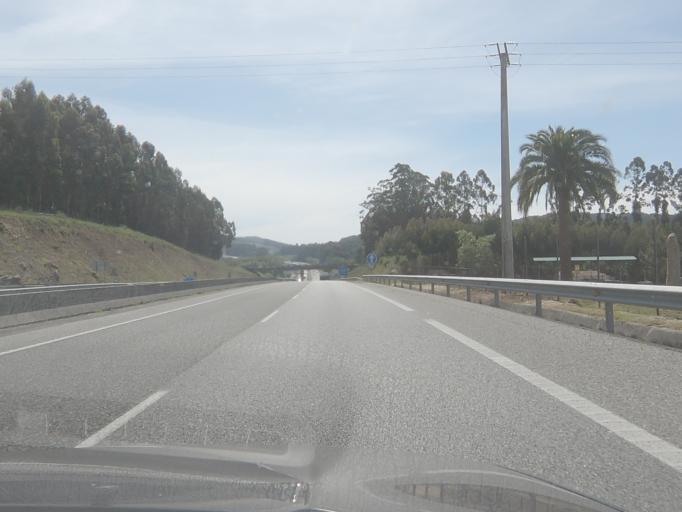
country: ES
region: Galicia
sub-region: Provincia de Pontevedra
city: Ribadumia
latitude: 42.5133
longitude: -8.7046
